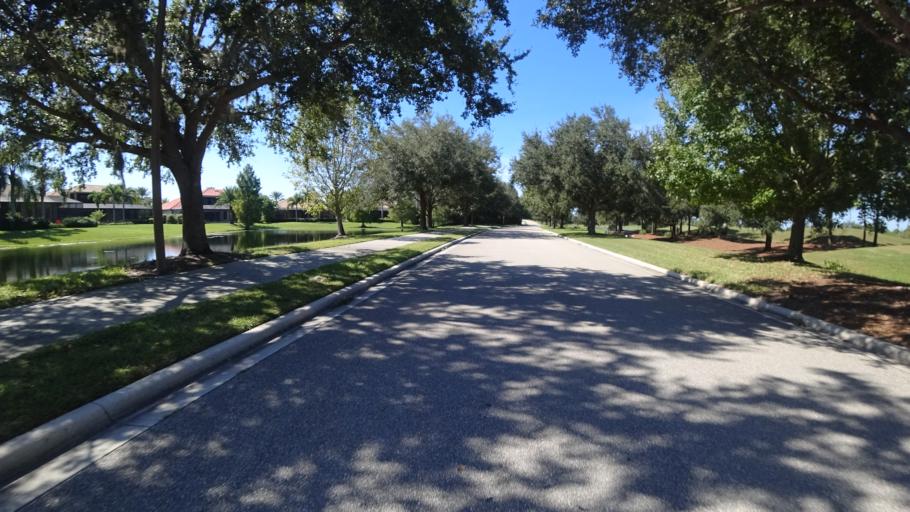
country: US
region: Florida
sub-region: Sarasota County
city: The Meadows
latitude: 27.4030
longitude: -82.4066
